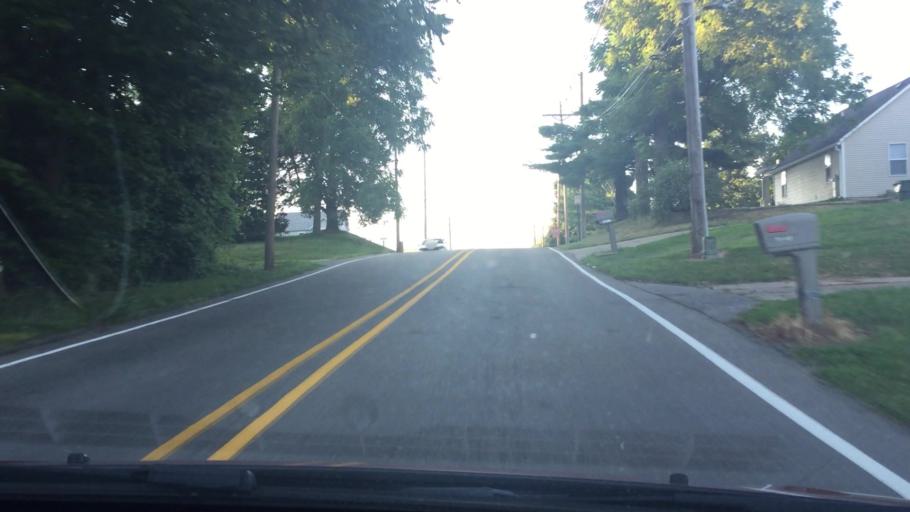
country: US
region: Iowa
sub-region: Muscatine County
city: Muscatine
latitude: 41.4300
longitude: -91.0649
